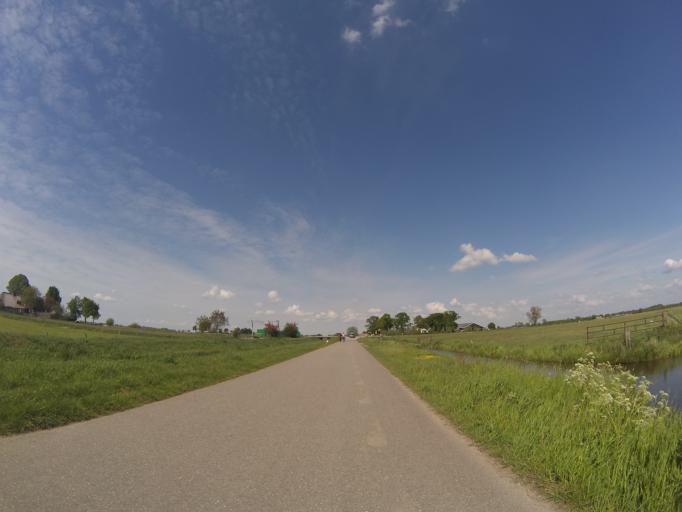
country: NL
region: Utrecht
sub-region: Gemeente Soest
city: Soest
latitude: 52.1805
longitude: 5.3258
